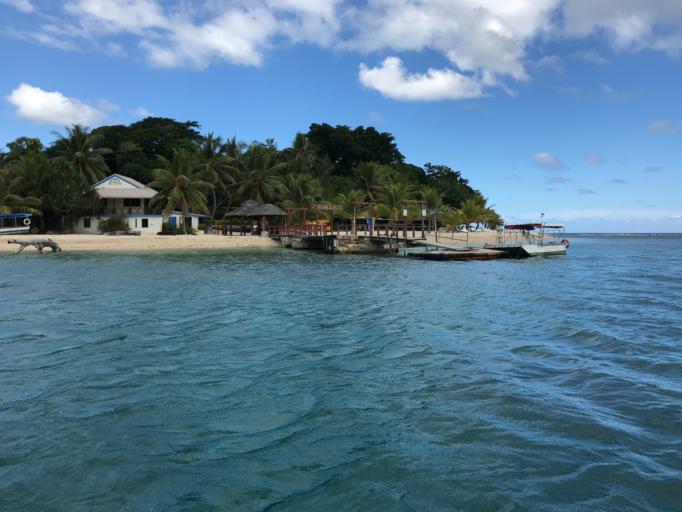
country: VU
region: Shefa
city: Port-Vila
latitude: -17.6956
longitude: 168.2634
